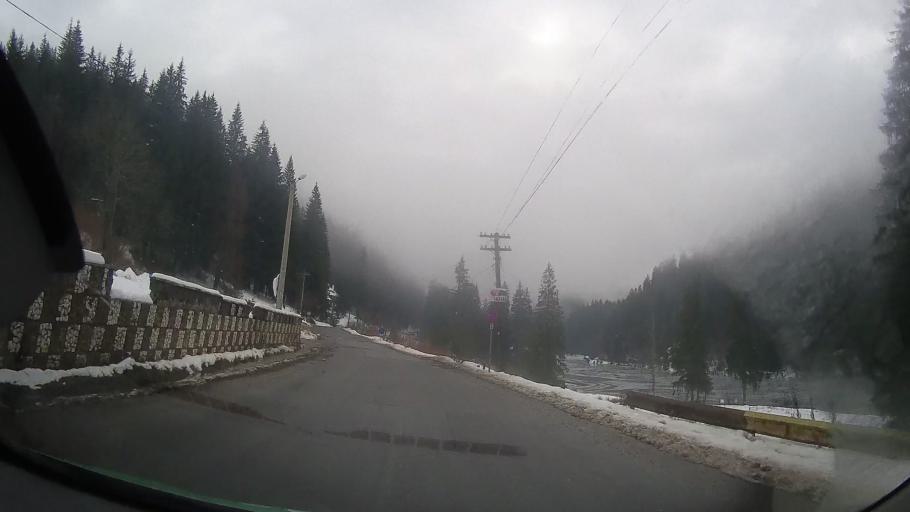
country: RO
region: Neamt
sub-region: Comuna Bicaz Chei
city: Bicaz Chei
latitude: 46.7898
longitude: 25.7885
